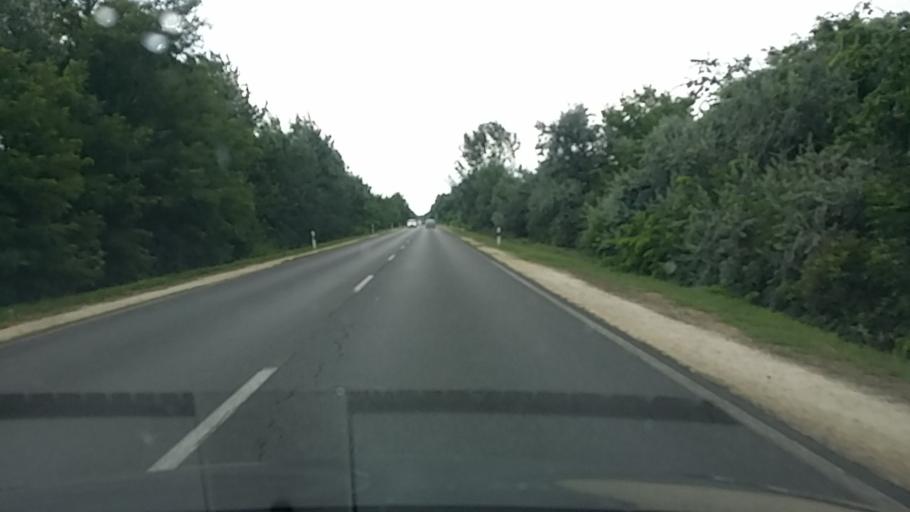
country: HU
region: Pest
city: Orkeny
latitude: 47.1135
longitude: 19.4512
